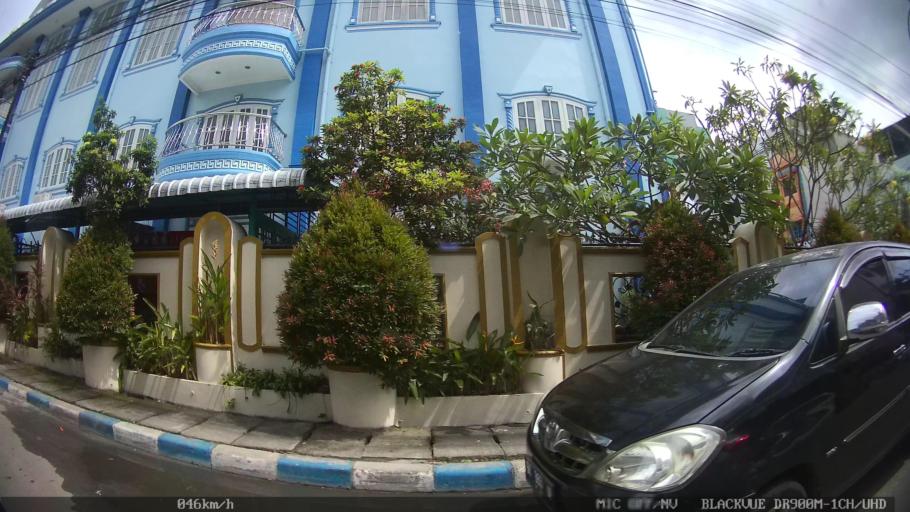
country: ID
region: North Sumatra
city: Percut
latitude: 3.5641
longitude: 98.8760
